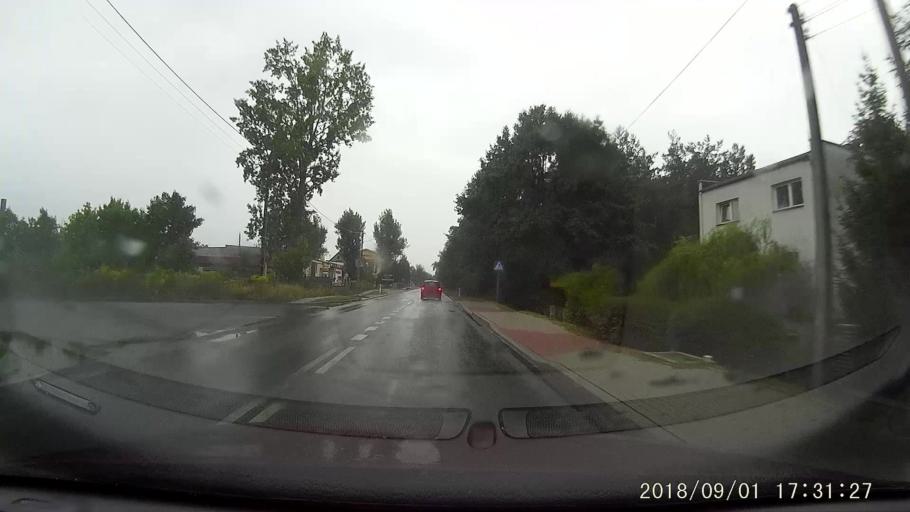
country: PL
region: Lubusz
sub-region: Powiat zaganski
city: Zagan
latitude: 51.6332
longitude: 15.3245
